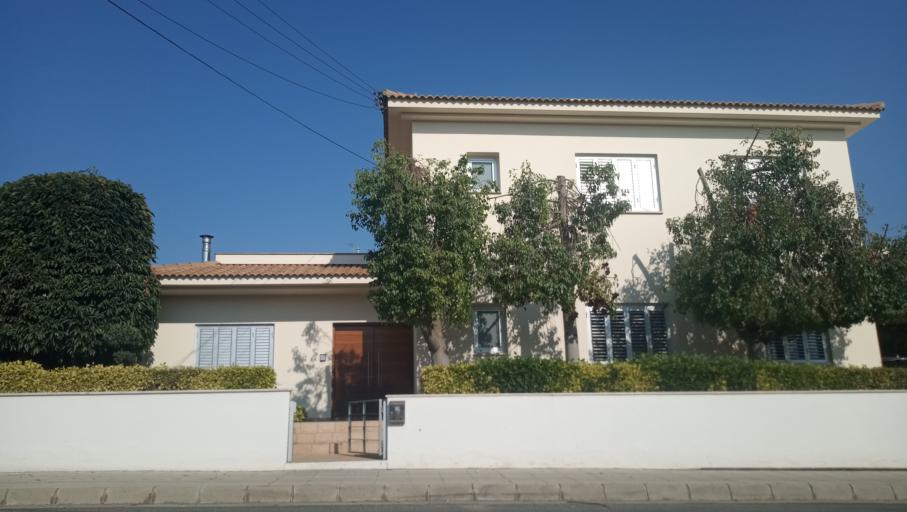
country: CY
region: Lefkosia
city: Nicosia
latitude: 35.1432
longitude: 33.3930
